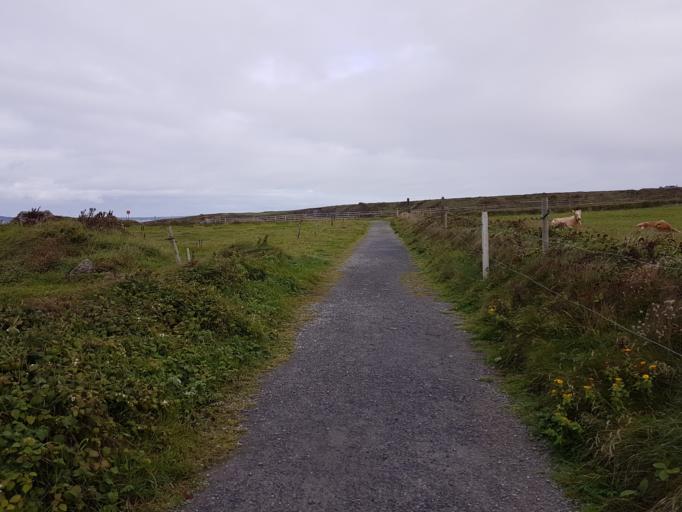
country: IE
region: Munster
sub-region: Ciarrai
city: Ballybunnion
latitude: 52.5164
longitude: -9.6777
